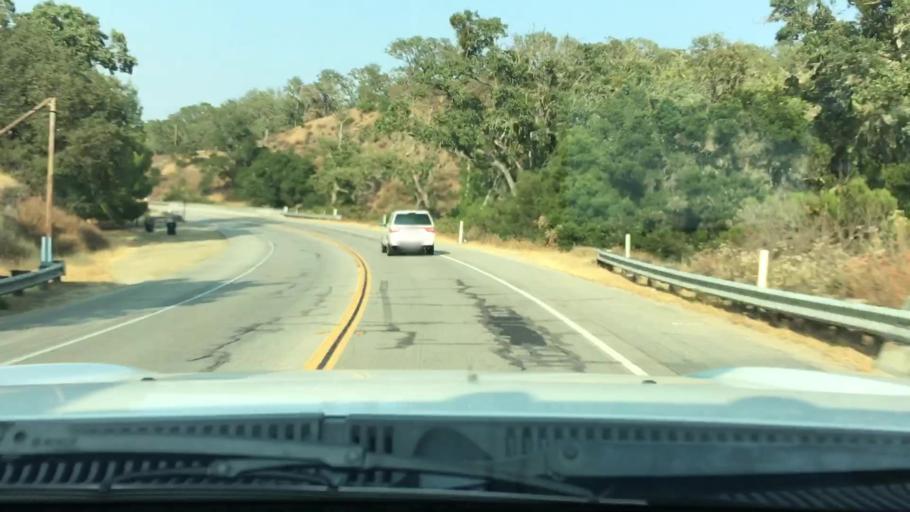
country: US
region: California
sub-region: San Luis Obispo County
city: Atascadero
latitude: 35.4564
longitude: -120.6892
